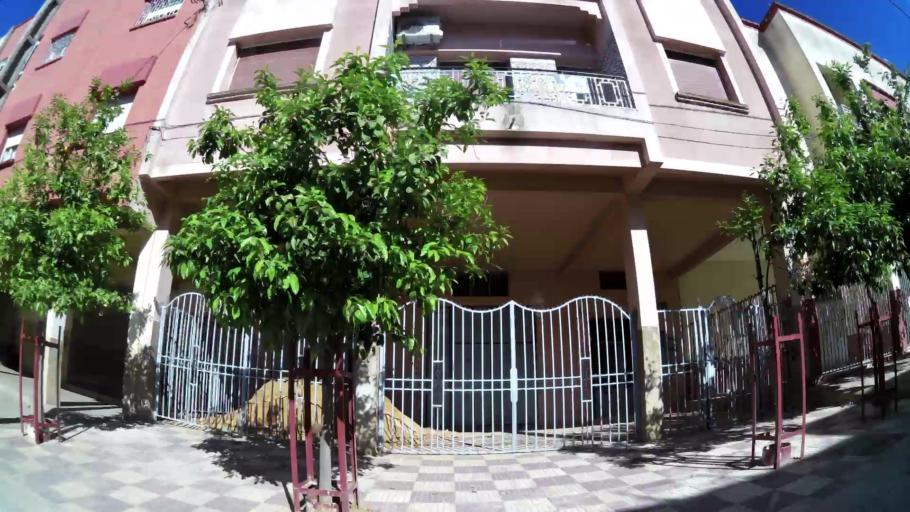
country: MA
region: Meknes-Tafilalet
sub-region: Meknes
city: Meknes
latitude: 33.8949
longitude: -5.4996
